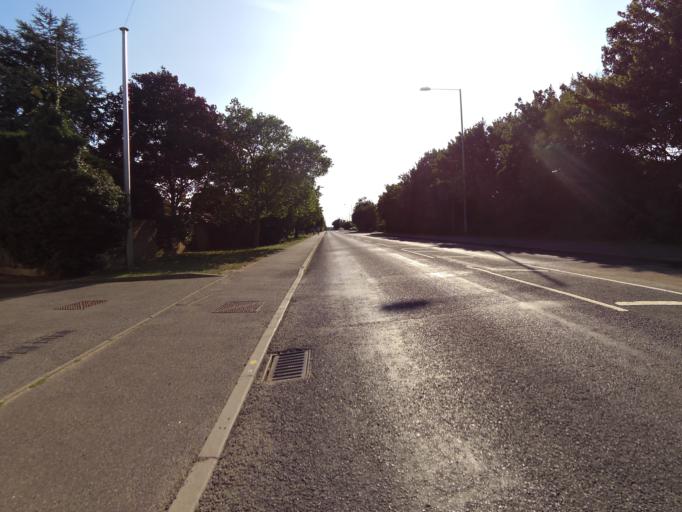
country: GB
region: England
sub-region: Essex
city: Hatfield Peverel
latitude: 51.7631
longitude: 0.5441
